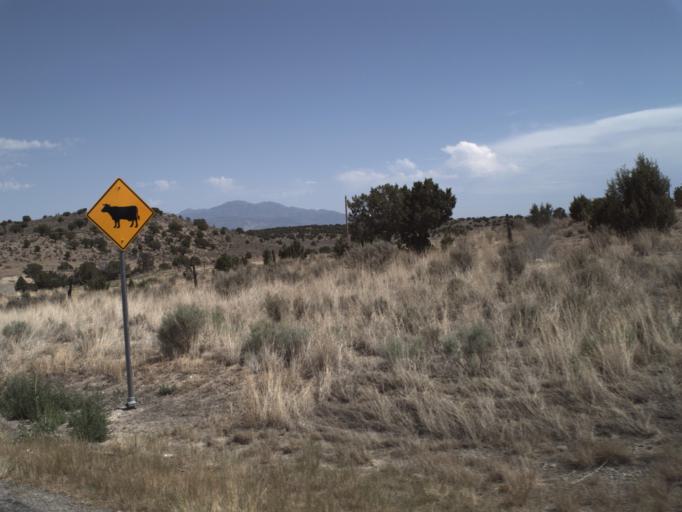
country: US
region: Utah
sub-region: Utah County
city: Eagle Mountain
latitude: 40.0443
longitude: -112.2922
